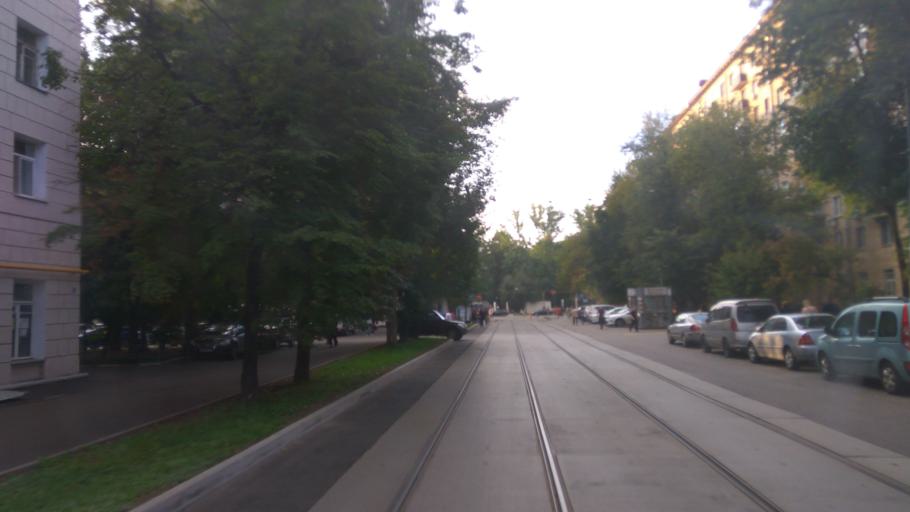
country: RU
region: Moskovskaya
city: Koptevo
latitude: 55.8172
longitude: 37.5023
